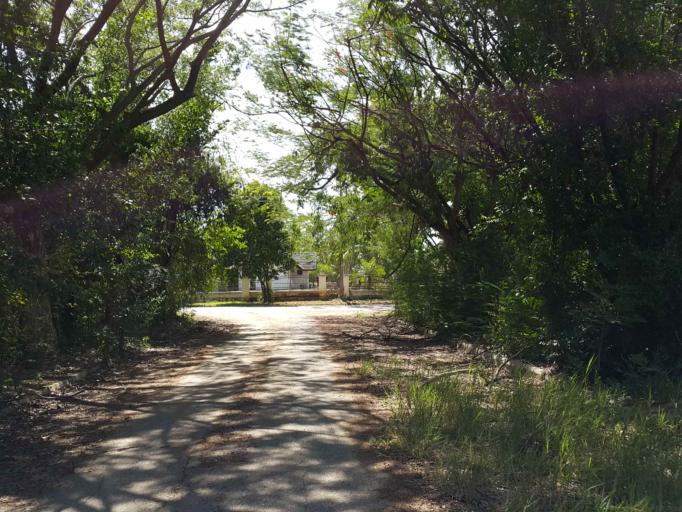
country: TH
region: Chiang Mai
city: San Kamphaeng
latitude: 18.7580
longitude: 99.1135
